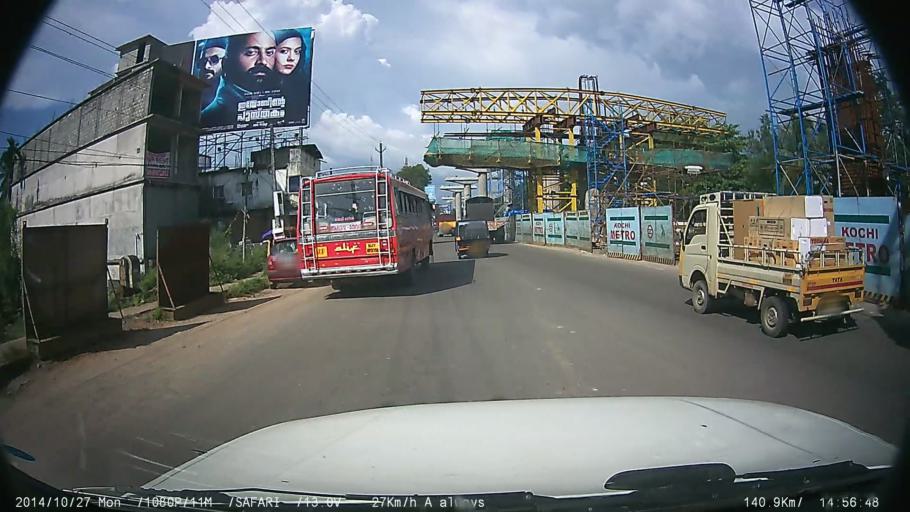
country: IN
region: Kerala
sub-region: Ernakulam
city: Elur
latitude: 10.0583
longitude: 76.3218
